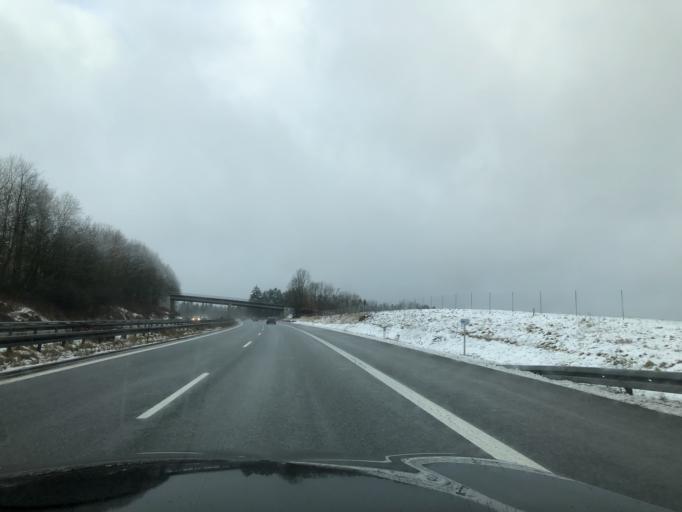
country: DE
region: Bavaria
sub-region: Upper Palatinate
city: Ursensollen
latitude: 49.4163
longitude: 11.7342
